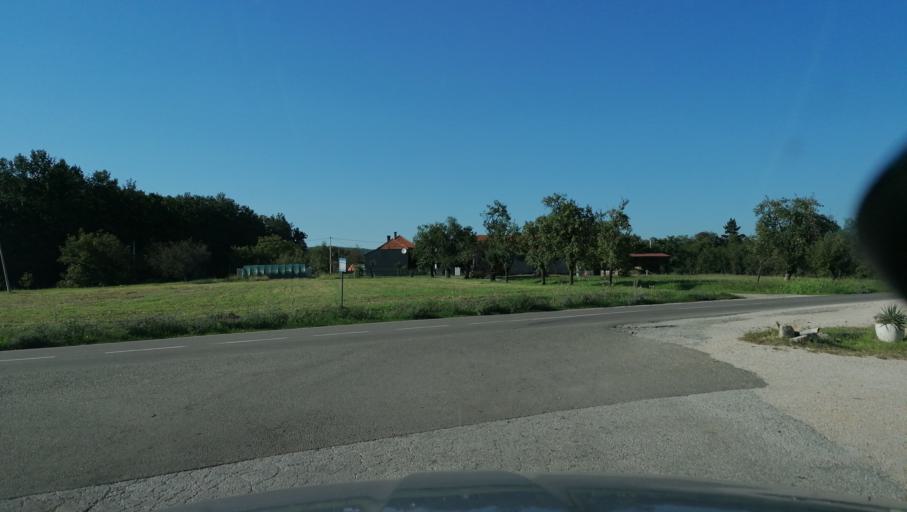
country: RS
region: Central Serbia
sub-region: Sumadijski Okrug
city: Knic
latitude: 43.8926
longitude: 20.6153
